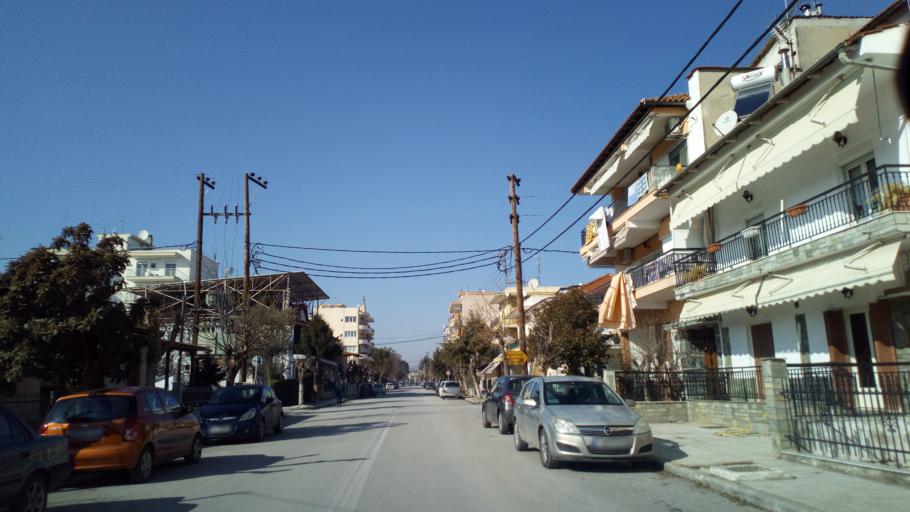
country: GR
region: Central Macedonia
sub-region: Nomos Thessalonikis
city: Lagkadas
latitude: 40.7452
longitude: 23.0741
